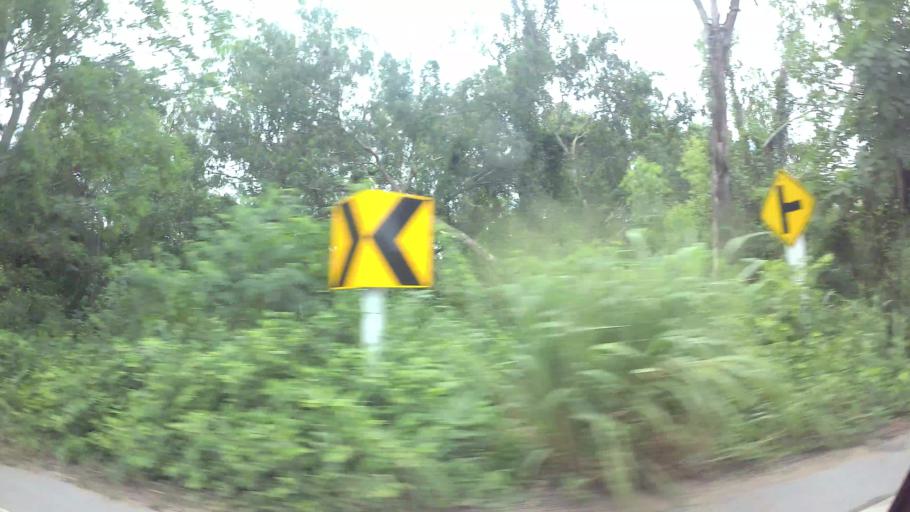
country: TH
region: Chon Buri
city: Si Racha
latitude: 13.1871
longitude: 100.9808
